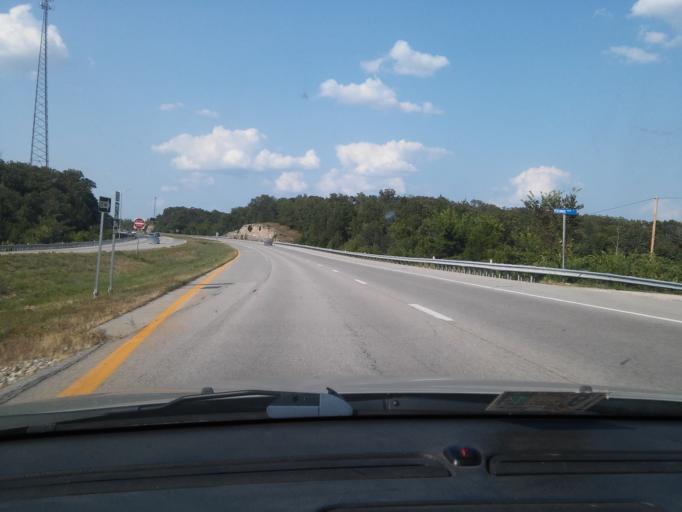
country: US
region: Missouri
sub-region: Cole County
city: Wardsville
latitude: 38.4759
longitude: -92.2752
